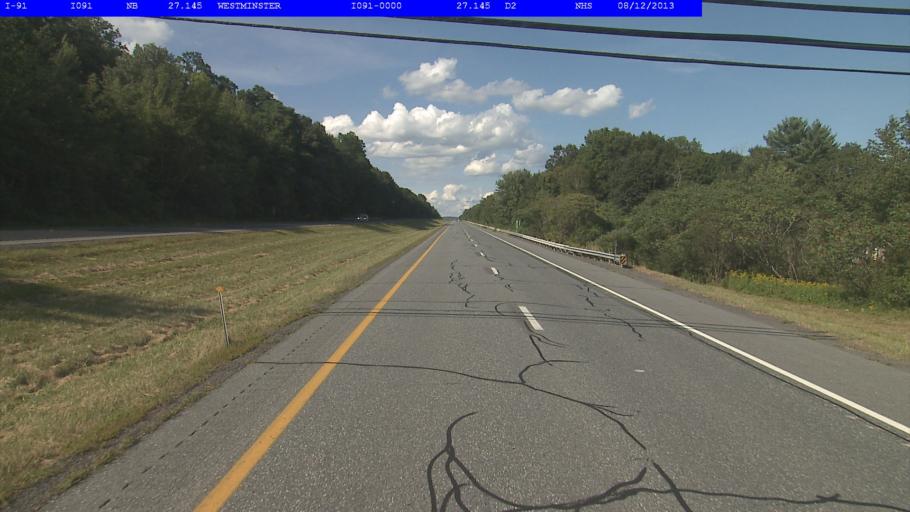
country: US
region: Vermont
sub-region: Windham County
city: Bellows Falls
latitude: 43.0718
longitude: -72.4681
